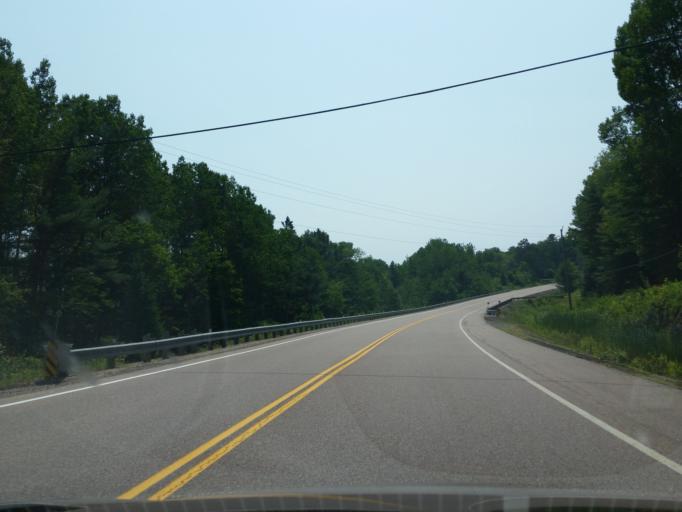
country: CA
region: Ontario
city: Deep River
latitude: 46.2095
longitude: -77.8877
